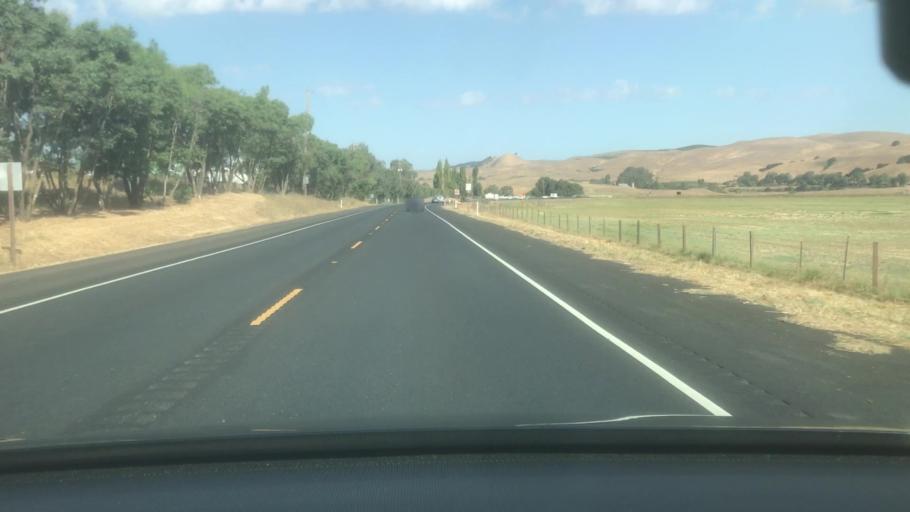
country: US
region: California
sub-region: Marin County
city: Black Point-Green Point
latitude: 38.1650
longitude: -122.4551
